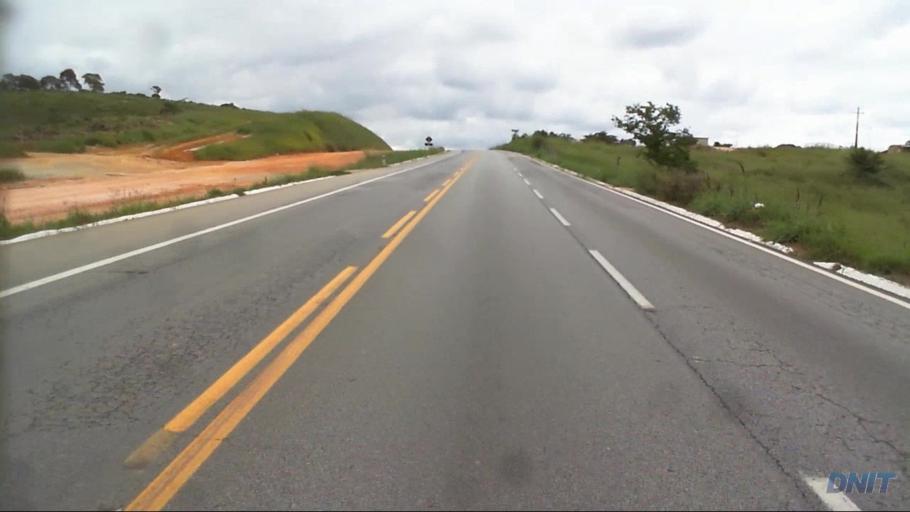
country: BR
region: Minas Gerais
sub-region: Barao De Cocais
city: Barao de Cocais
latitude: -19.7808
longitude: -43.4371
